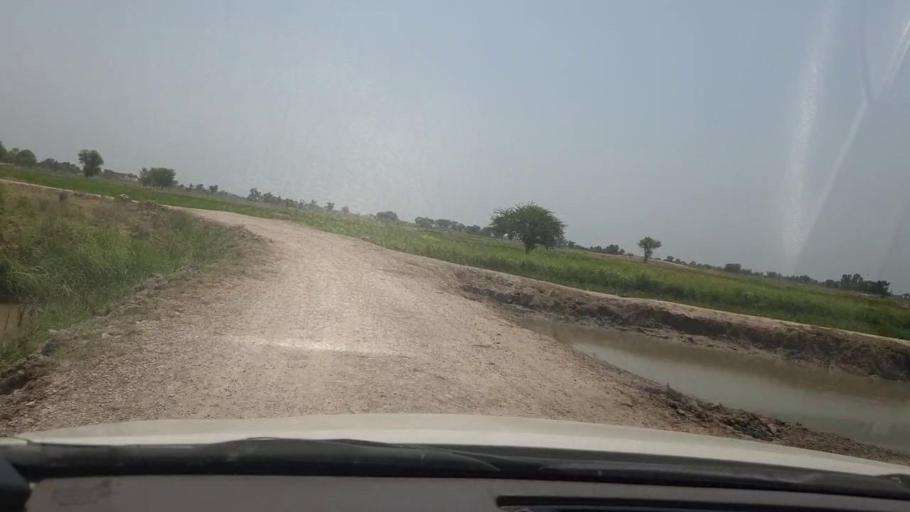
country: PK
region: Sindh
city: Garhi Yasin
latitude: 27.9177
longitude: 68.5546
